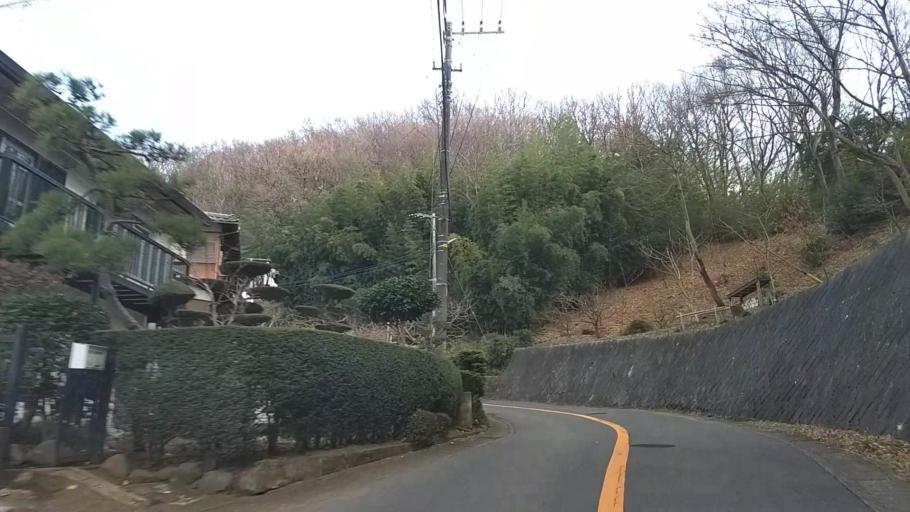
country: JP
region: Kanagawa
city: Isehara
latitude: 35.4212
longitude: 139.3133
